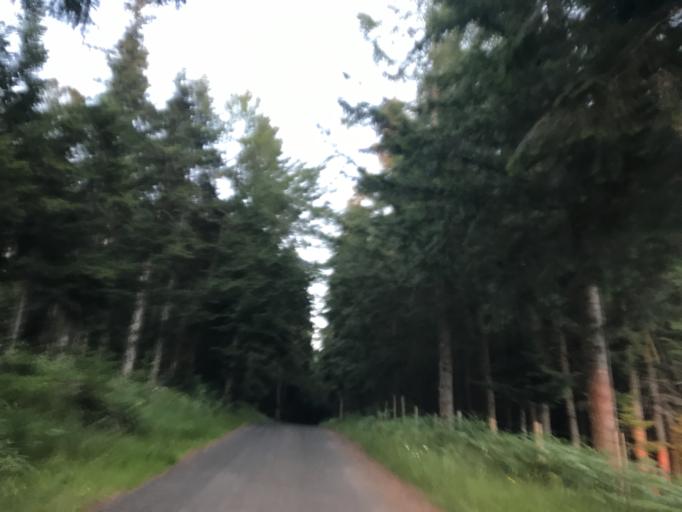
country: FR
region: Rhone-Alpes
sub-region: Departement de la Loire
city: Noiretable
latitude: 45.7655
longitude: 3.7179
